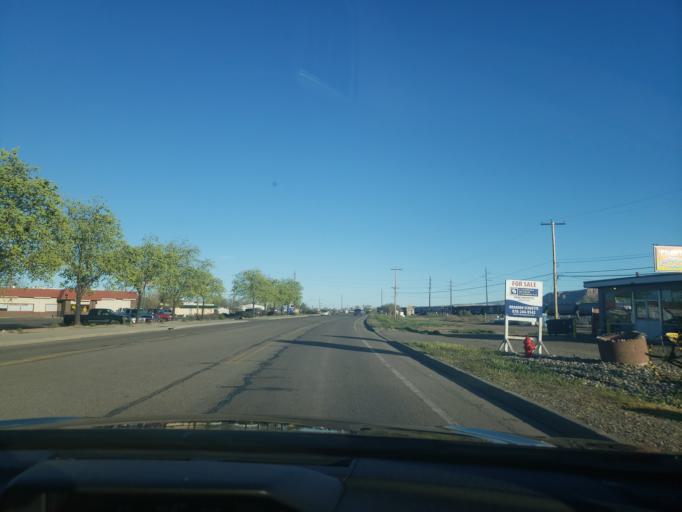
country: US
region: Colorado
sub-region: Mesa County
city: Fruita
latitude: 39.1546
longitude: -108.7305
